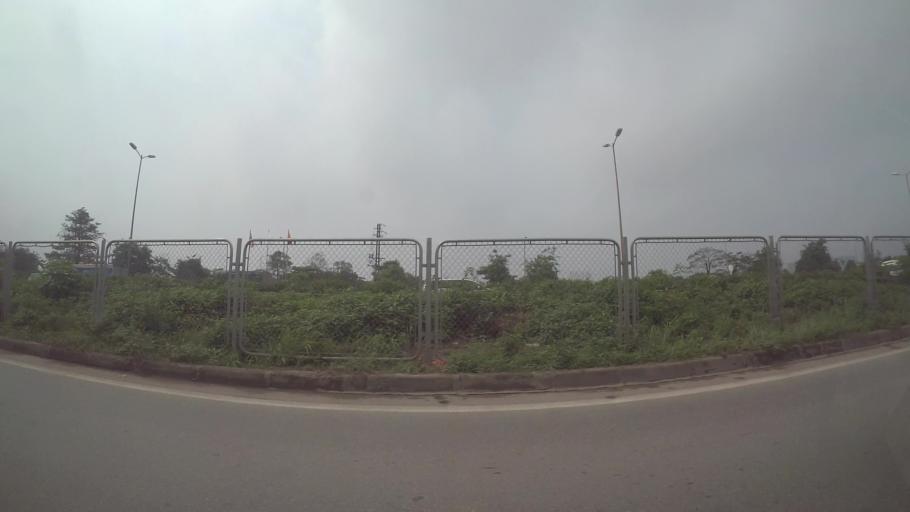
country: VN
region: Ha Noi
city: Van Dien
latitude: 20.9647
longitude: 105.8587
